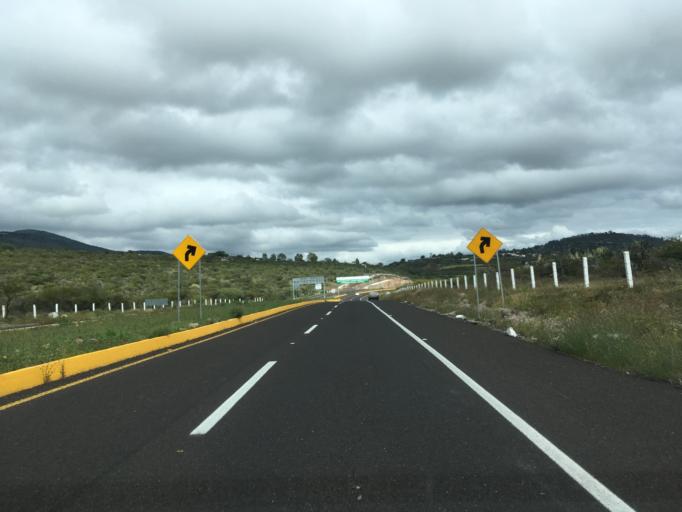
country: MX
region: Hidalgo
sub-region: Atotonilco el Grande
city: Santa Maria Amajac
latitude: 20.3856
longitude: -98.7235
